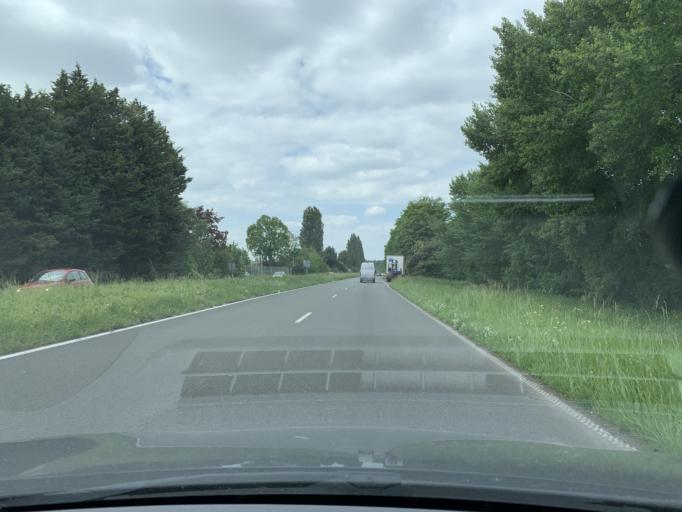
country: FR
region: Nord-Pas-de-Calais
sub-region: Departement du Nord
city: Cuincy
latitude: 50.3785
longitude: 3.0599
